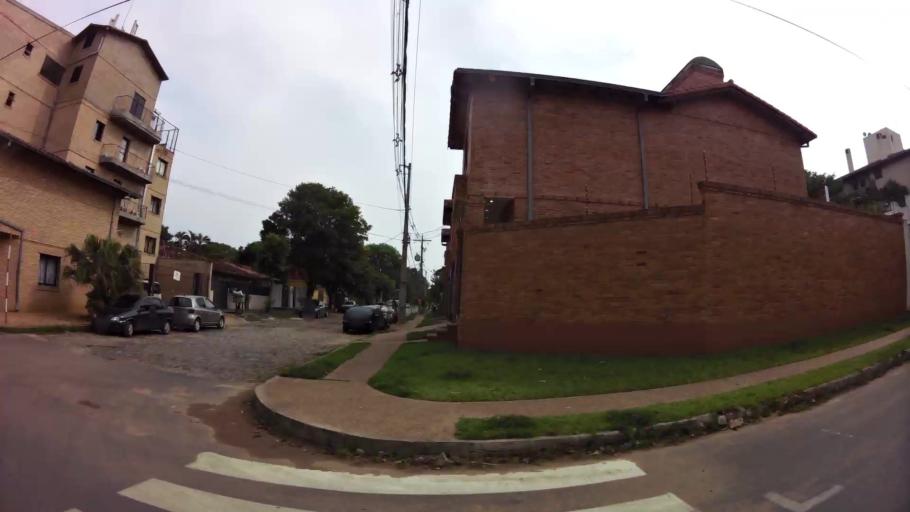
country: PY
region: Central
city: Fernando de la Mora
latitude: -25.3014
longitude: -57.5559
